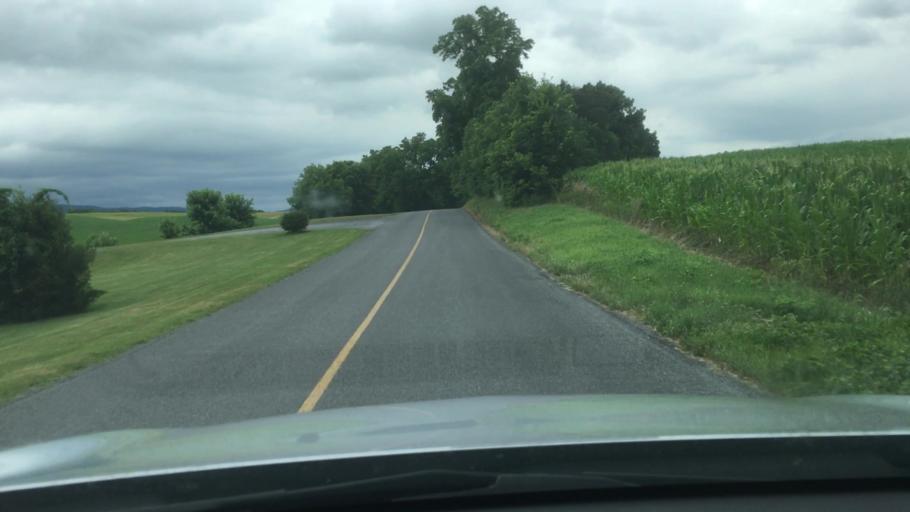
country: US
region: Pennsylvania
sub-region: Franklin County
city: Greencastle
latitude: 39.8606
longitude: -77.7994
